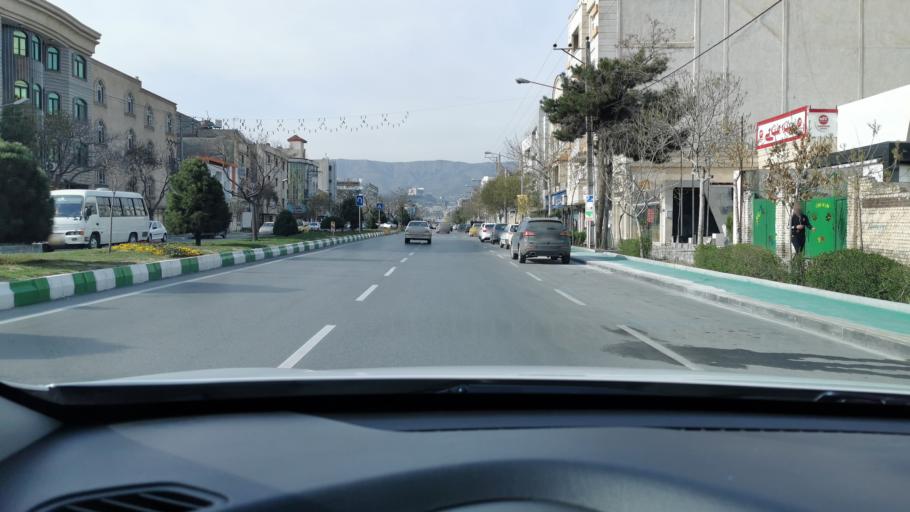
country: IR
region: Razavi Khorasan
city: Mashhad
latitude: 36.3185
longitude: 59.5113
